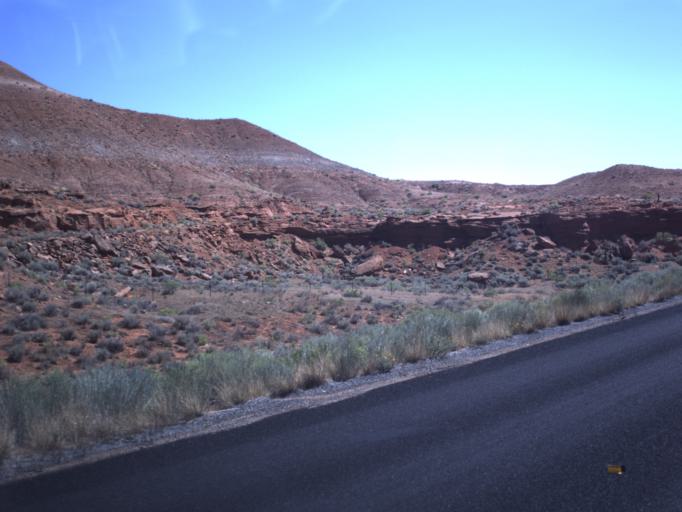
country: US
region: Utah
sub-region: Uintah County
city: Maeser
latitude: 40.4154
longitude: -109.7515
